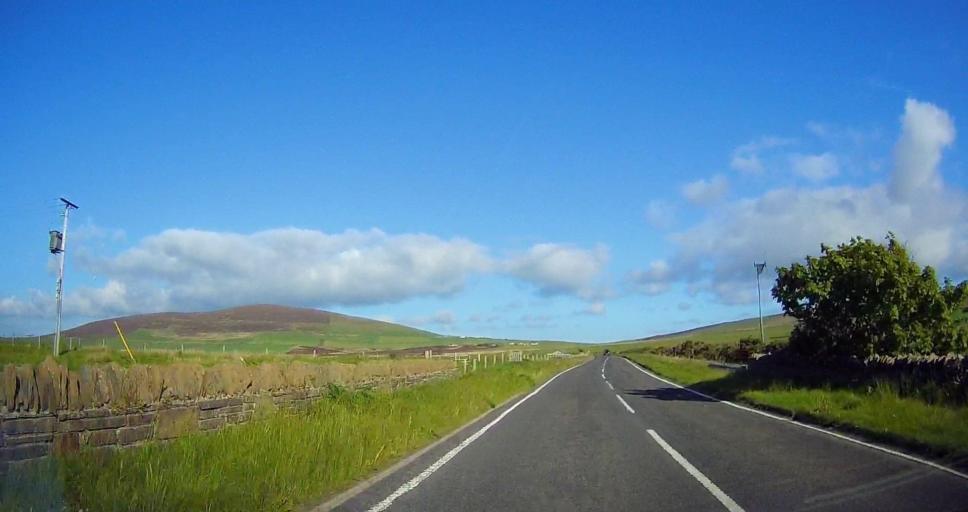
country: GB
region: Scotland
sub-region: Orkney Islands
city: Orkney
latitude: 58.9912
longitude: -3.0703
